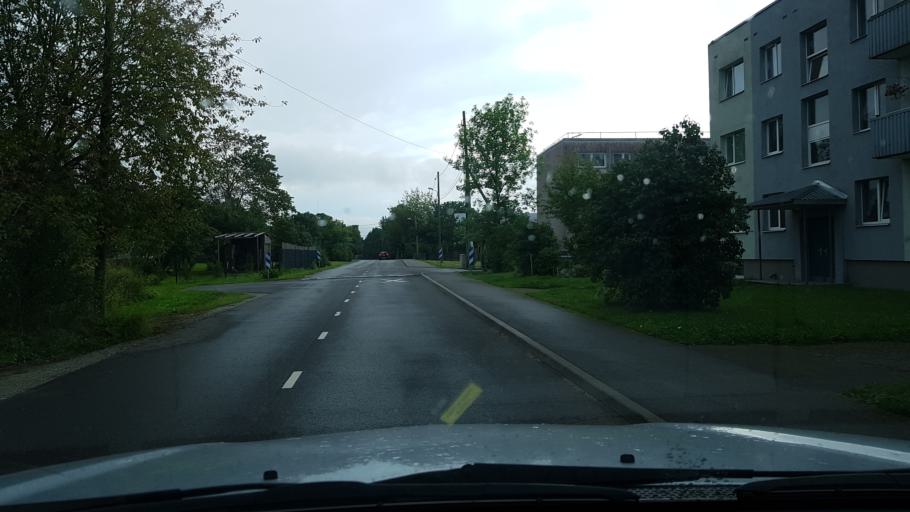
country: EE
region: Harju
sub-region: Joelaehtme vald
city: Loo
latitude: 59.4030
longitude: 24.9304
